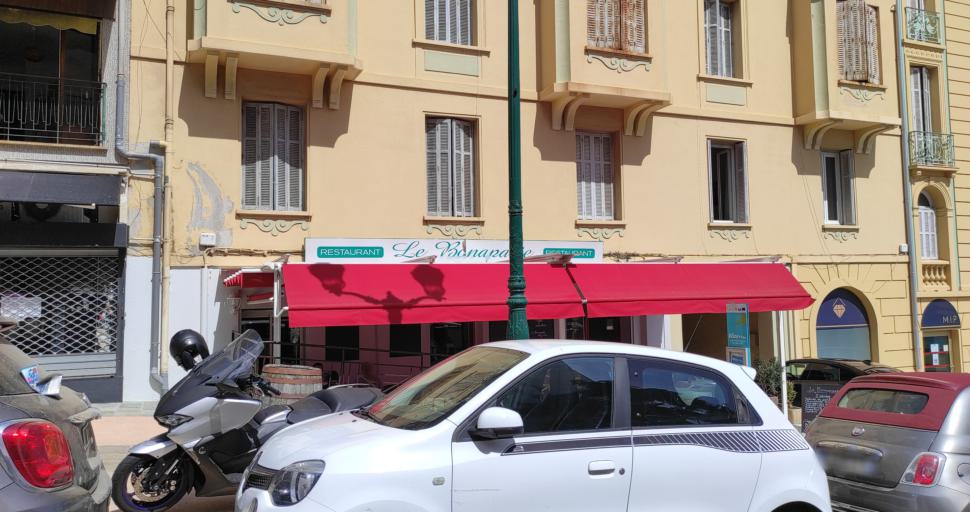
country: FR
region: Corsica
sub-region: Departement de la Corse-du-Sud
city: Ajaccio
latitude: 41.9132
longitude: 8.7255
